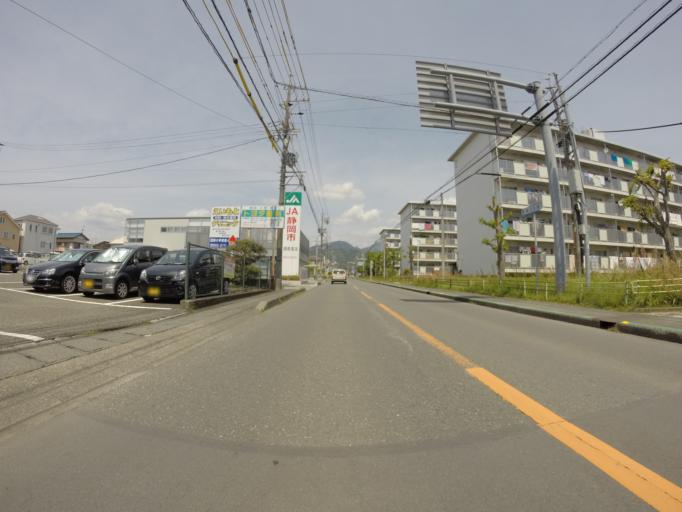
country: JP
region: Shizuoka
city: Shizuoka-shi
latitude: 35.0119
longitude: 138.4246
